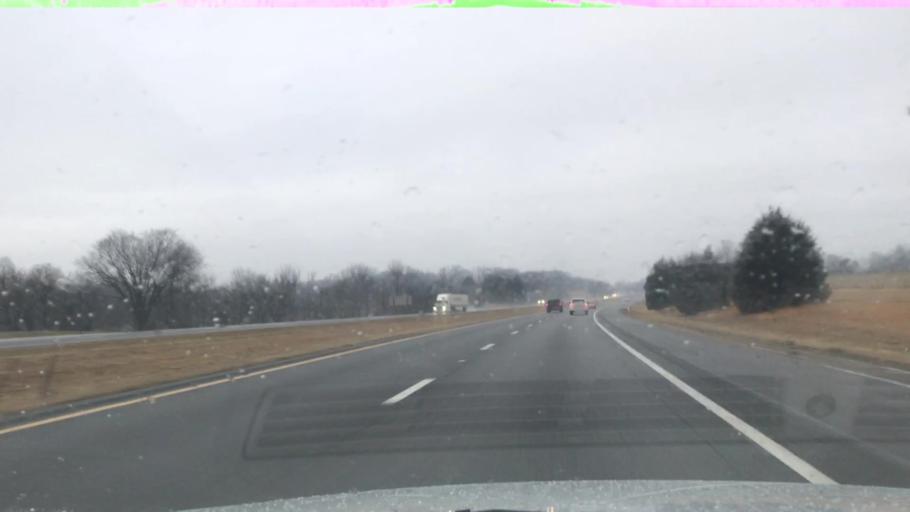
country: US
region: Kentucky
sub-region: Christian County
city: Oak Grove
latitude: 36.6390
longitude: -87.3363
